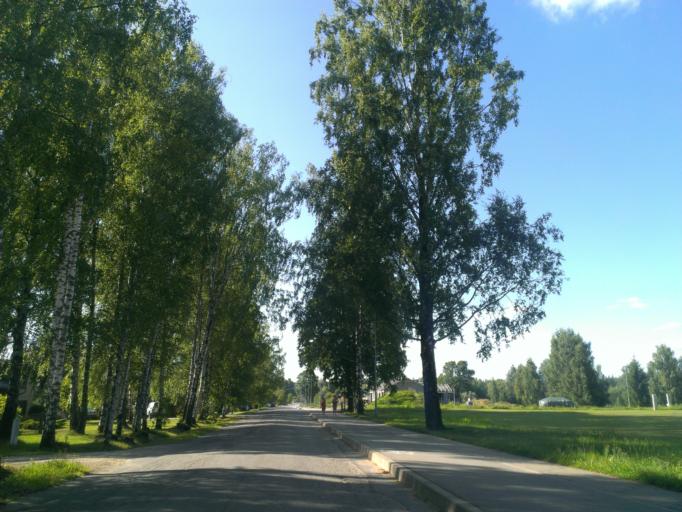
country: LV
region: Sigulda
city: Sigulda
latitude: 57.1648
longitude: 24.8766
